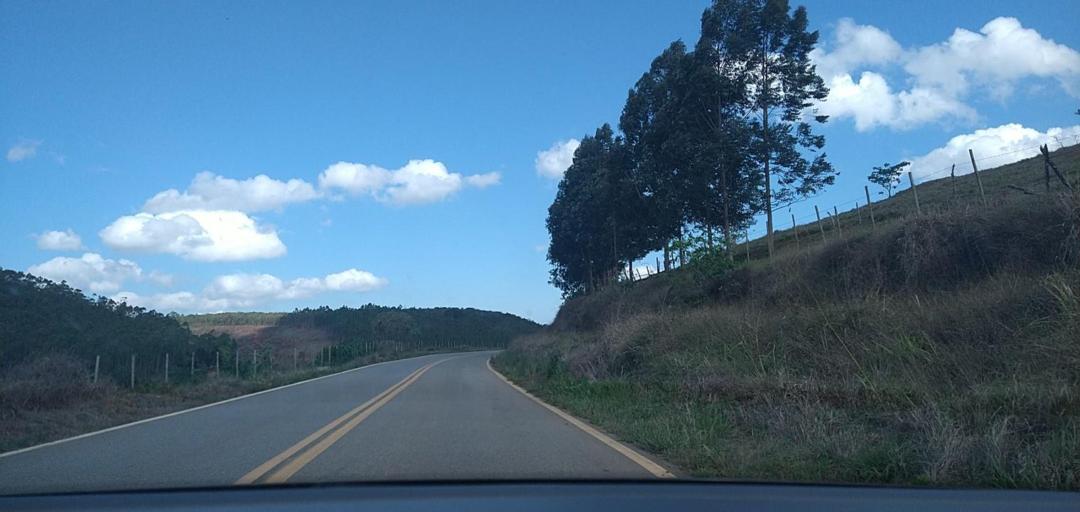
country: BR
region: Minas Gerais
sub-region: Alvinopolis
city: Alvinopolis
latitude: -20.0191
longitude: -43.0687
